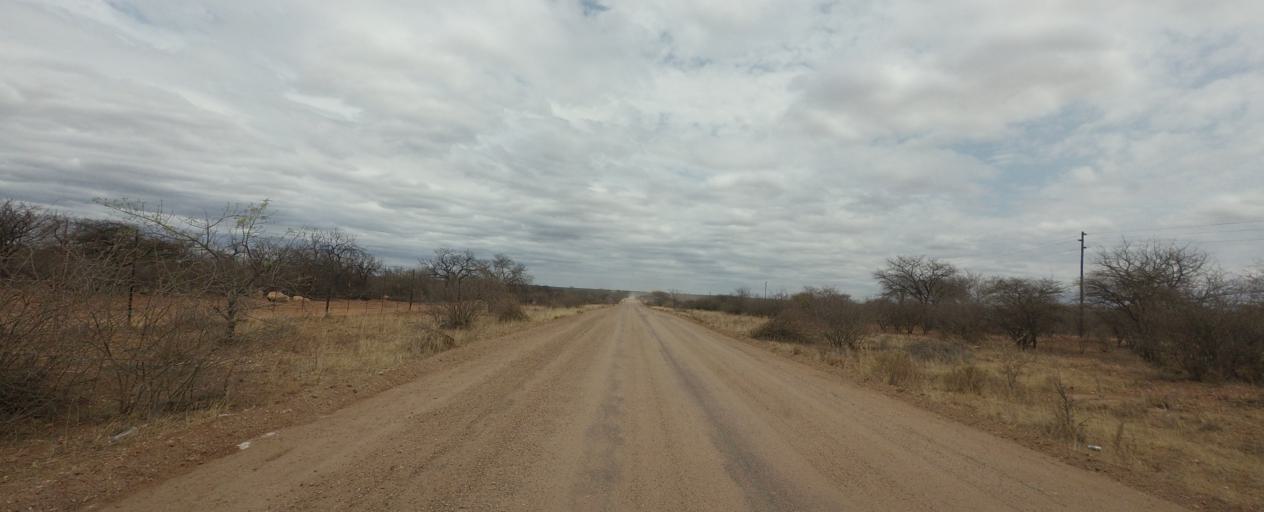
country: BW
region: Central
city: Mathathane
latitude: -22.6785
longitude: 28.6651
